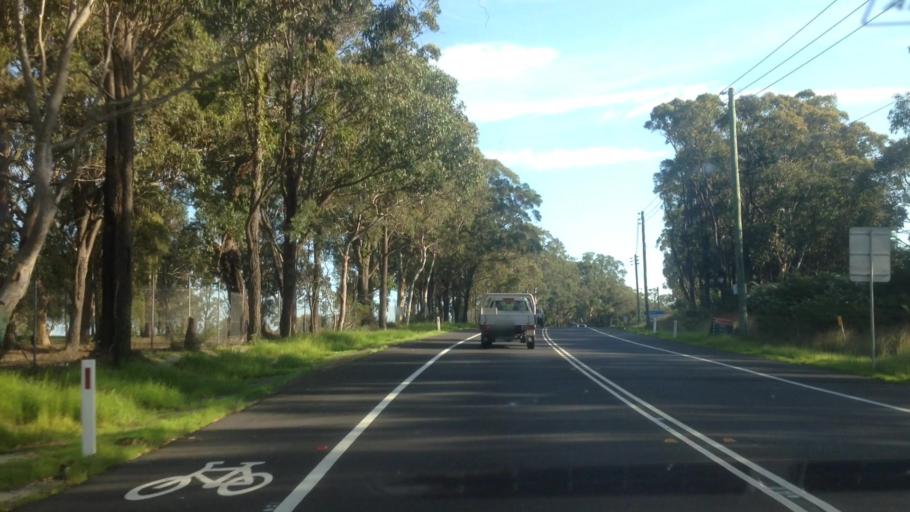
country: AU
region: New South Wales
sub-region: Lake Macquarie Shire
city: Dora Creek
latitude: -33.1173
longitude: 151.4783
